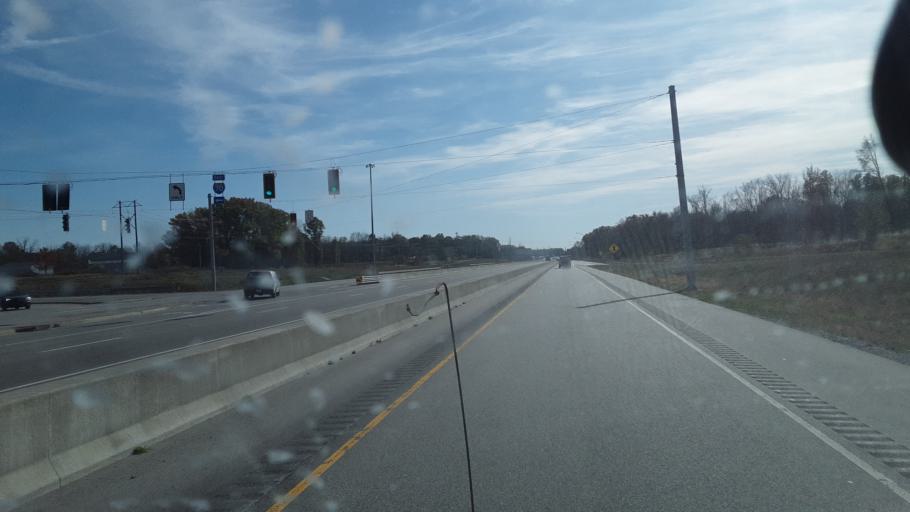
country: US
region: Indiana
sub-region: Vigo County
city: Terre Haute
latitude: 39.4299
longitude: -87.3333
